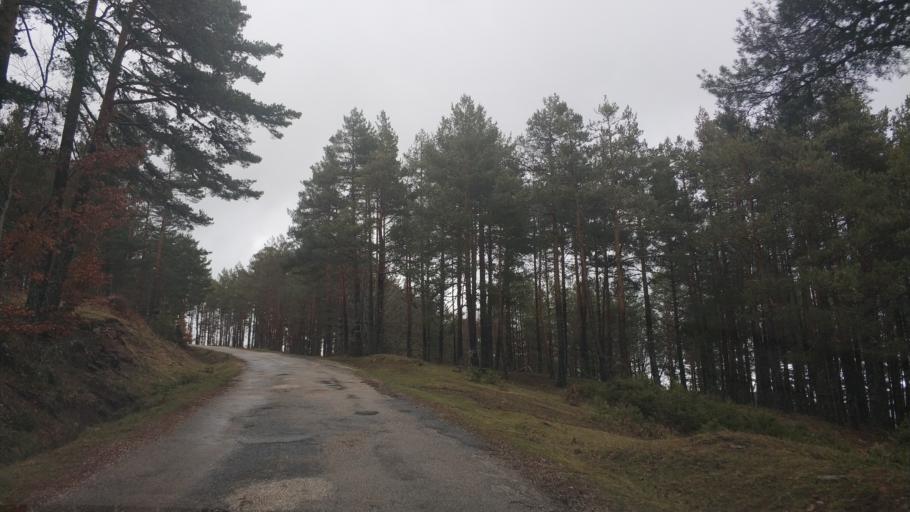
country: ES
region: Castille and Leon
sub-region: Provincia de Burgos
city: Neila
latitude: 42.0434
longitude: -3.0124
